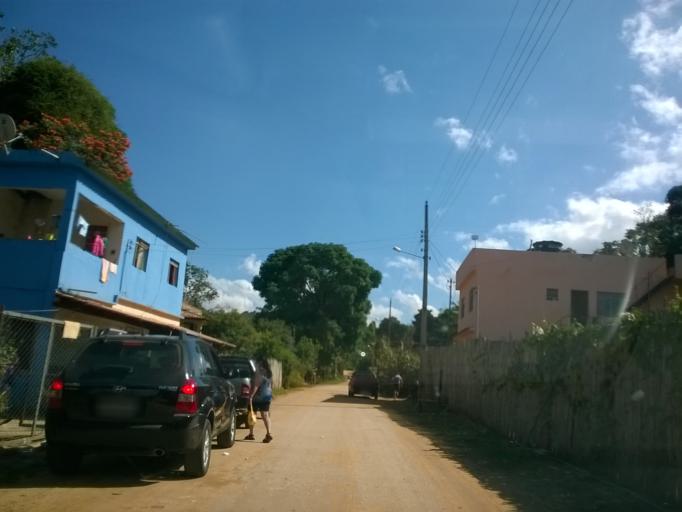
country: BR
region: Minas Gerais
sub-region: Uba
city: Uba
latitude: -21.0712
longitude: -42.8984
